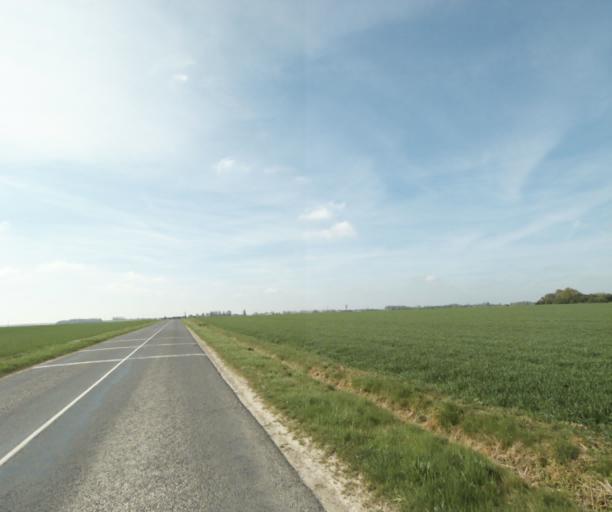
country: FR
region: Ile-de-France
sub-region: Departement de Seine-et-Marne
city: Nangis
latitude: 48.5727
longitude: 3.0392
